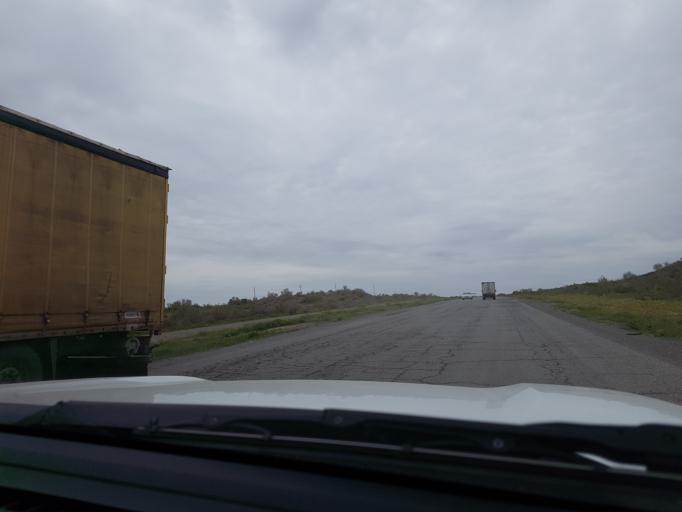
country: TM
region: Mary
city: Bayramaly
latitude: 37.8952
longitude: 62.6164
